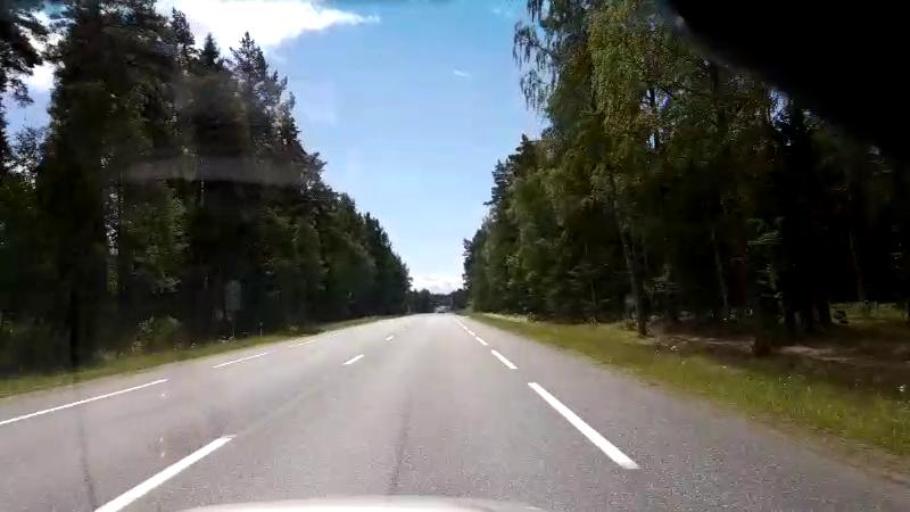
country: LV
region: Saulkrastu
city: Saulkrasti
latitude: 57.4724
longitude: 24.4345
